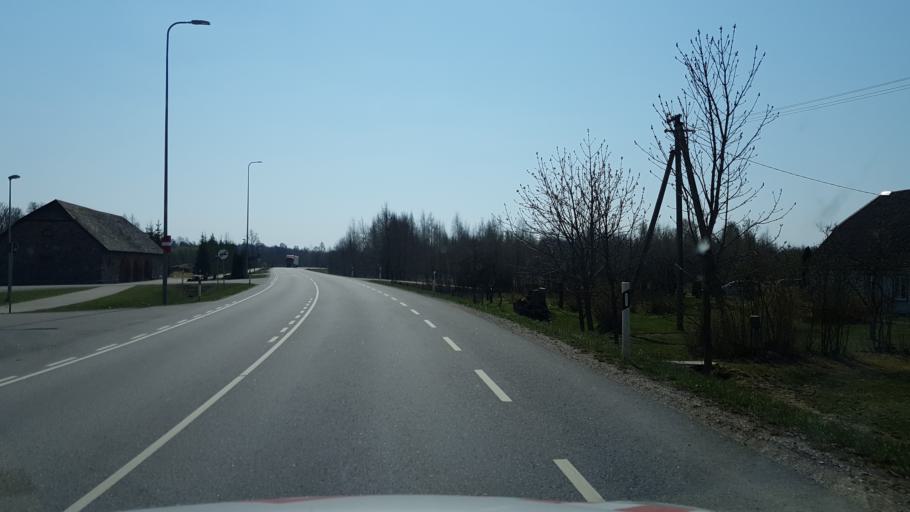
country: EE
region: Paernumaa
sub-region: Sauga vald
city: Sauga
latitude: 58.4298
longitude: 24.4384
